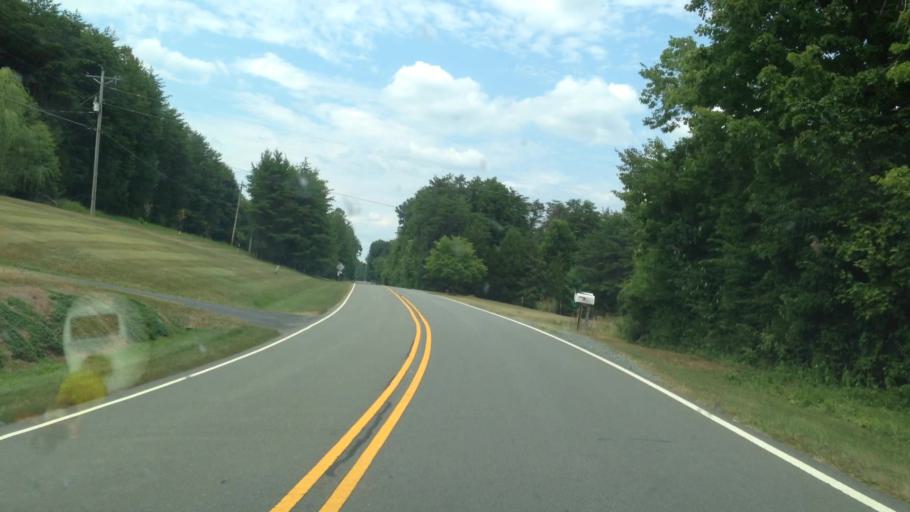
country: US
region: North Carolina
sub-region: Stokes County
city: Walnut Cove
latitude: 36.3887
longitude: -80.0953
